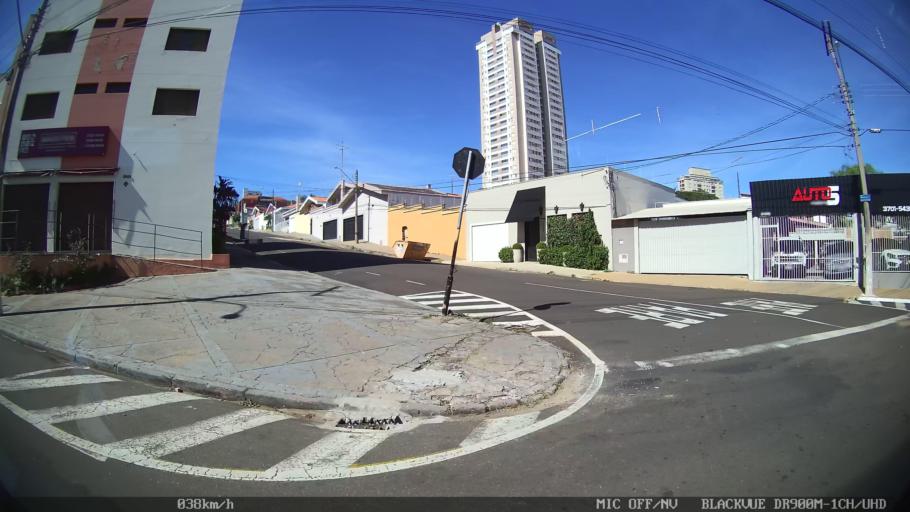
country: BR
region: Sao Paulo
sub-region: Franca
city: Franca
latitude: -20.5398
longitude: -47.3935
